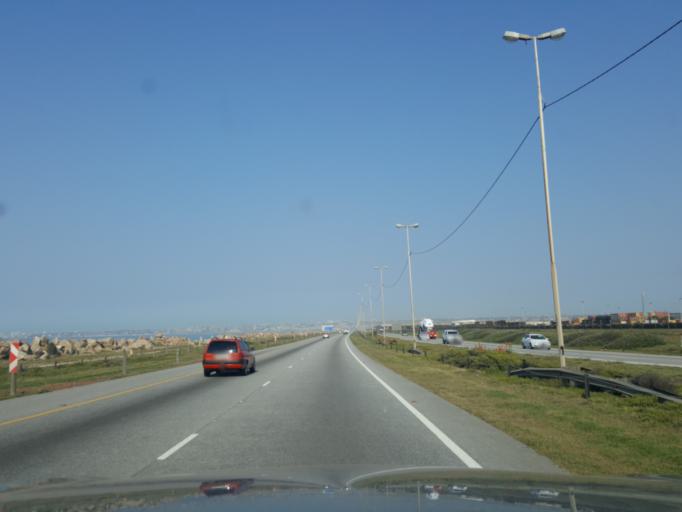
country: ZA
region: Eastern Cape
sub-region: Nelson Mandela Bay Metropolitan Municipality
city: Port Elizabeth
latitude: -33.8918
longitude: 25.6219
